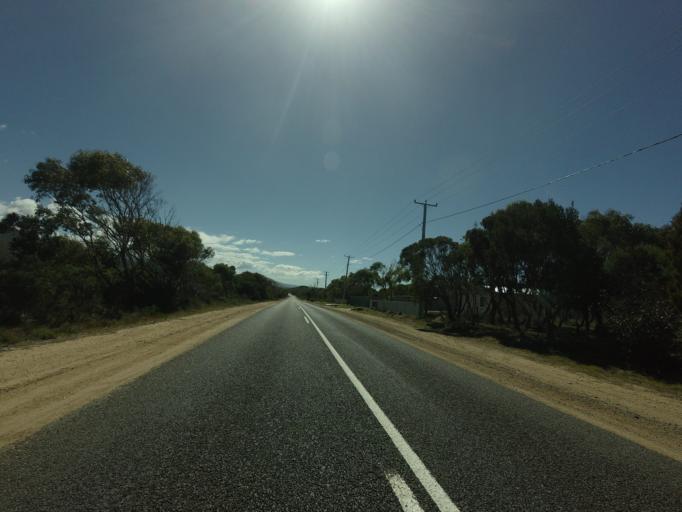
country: AU
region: Tasmania
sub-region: Break O'Day
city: St Helens
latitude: -41.8184
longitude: 148.2627
